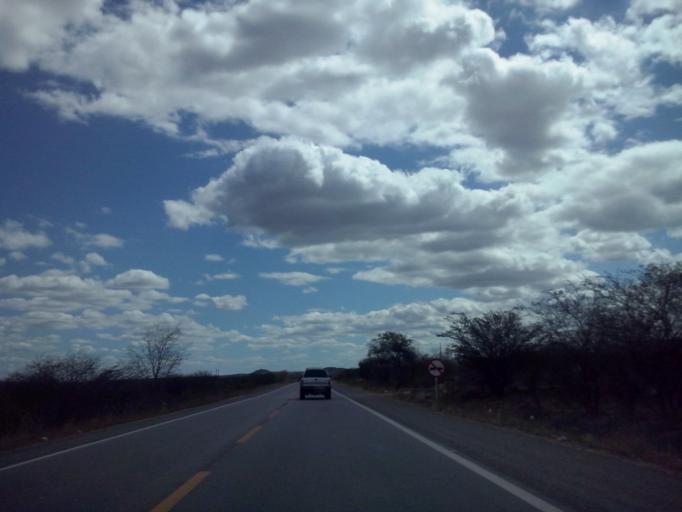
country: BR
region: Paraiba
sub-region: Soledade
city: Soledade
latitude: -7.0384
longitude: -36.4243
